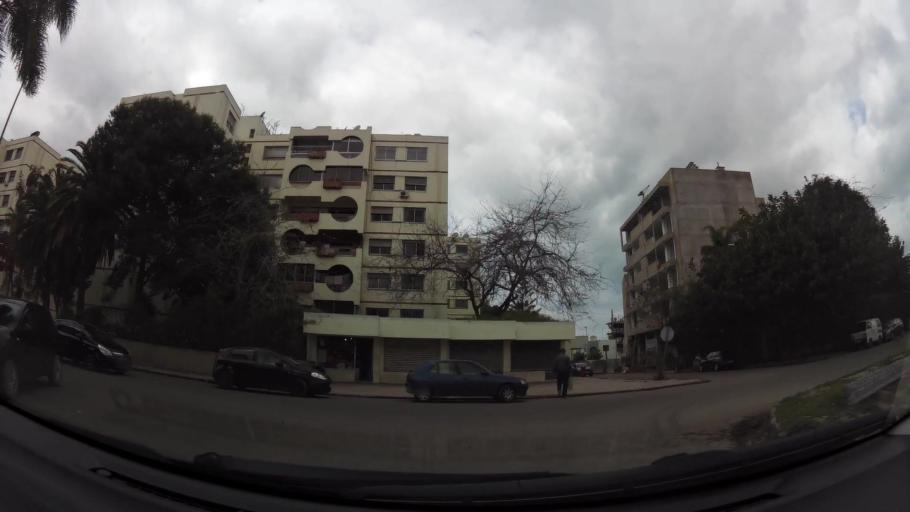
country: MA
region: Grand Casablanca
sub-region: Casablanca
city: Casablanca
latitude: 33.5783
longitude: -7.6490
